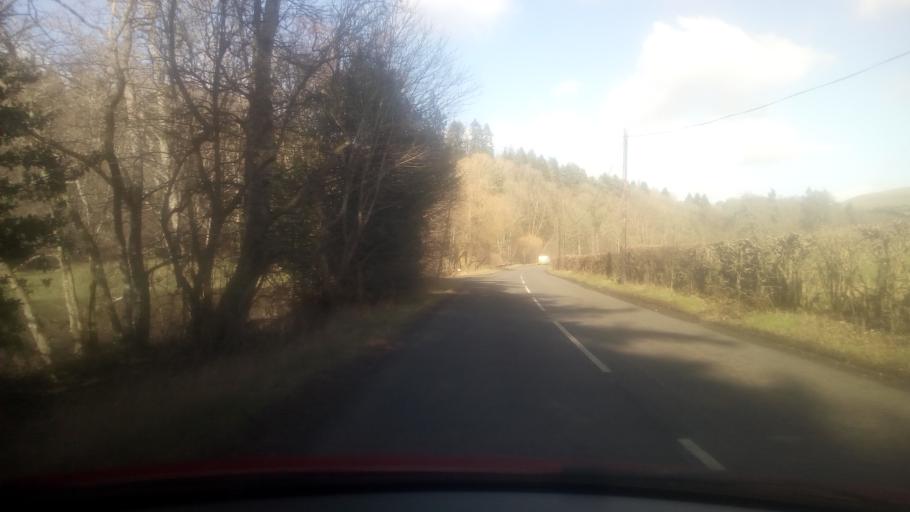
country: GB
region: Scotland
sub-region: The Scottish Borders
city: Selkirk
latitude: 55.5873
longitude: -2.8679
